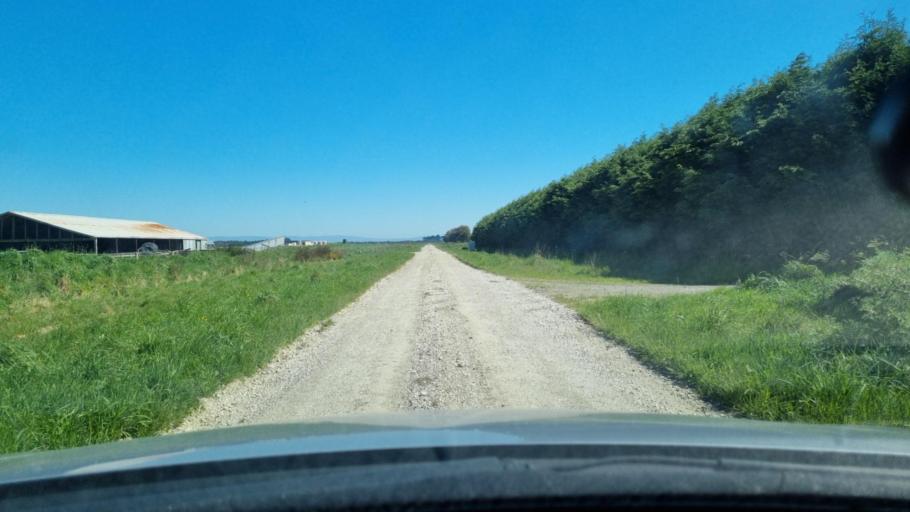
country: NZ
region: Southland
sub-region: Invercargill City
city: Invercargill
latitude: -46.4246
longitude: 168.3158
